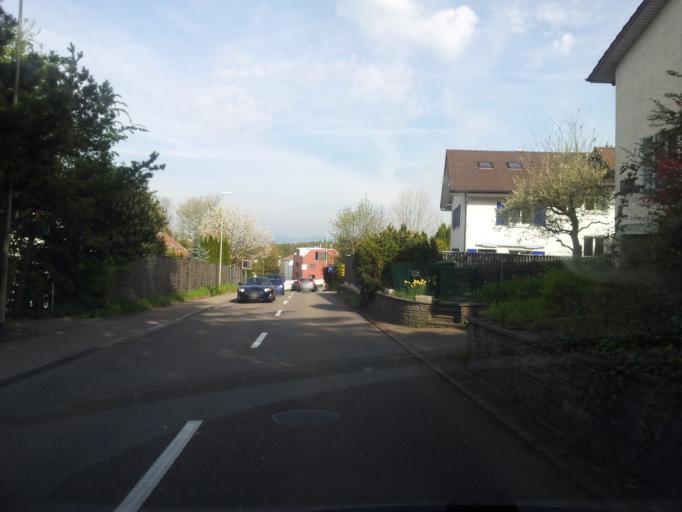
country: CH
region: Zurich
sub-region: Bezirk Uster
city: Gockhausen
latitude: 47.3820
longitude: 8.5946
